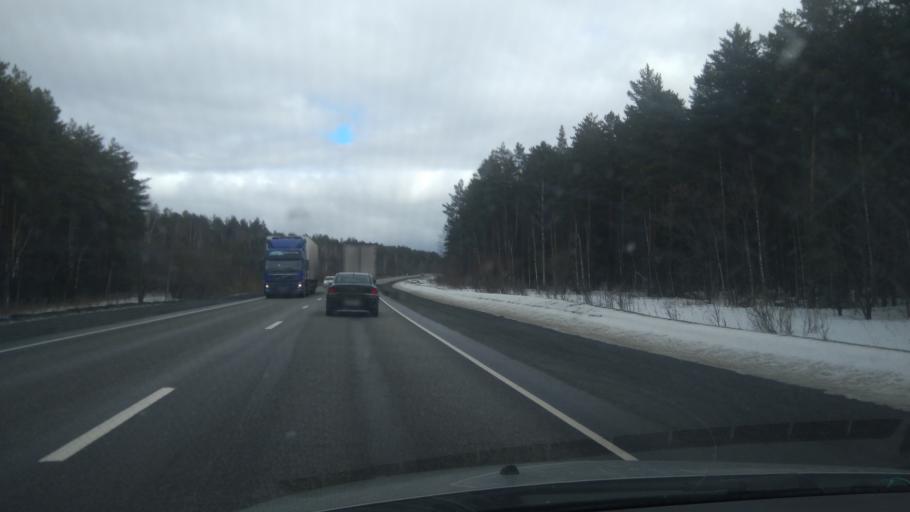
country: RU
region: Sverdlovsk
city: Bisert'
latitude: 56.8295
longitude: 58.7763
